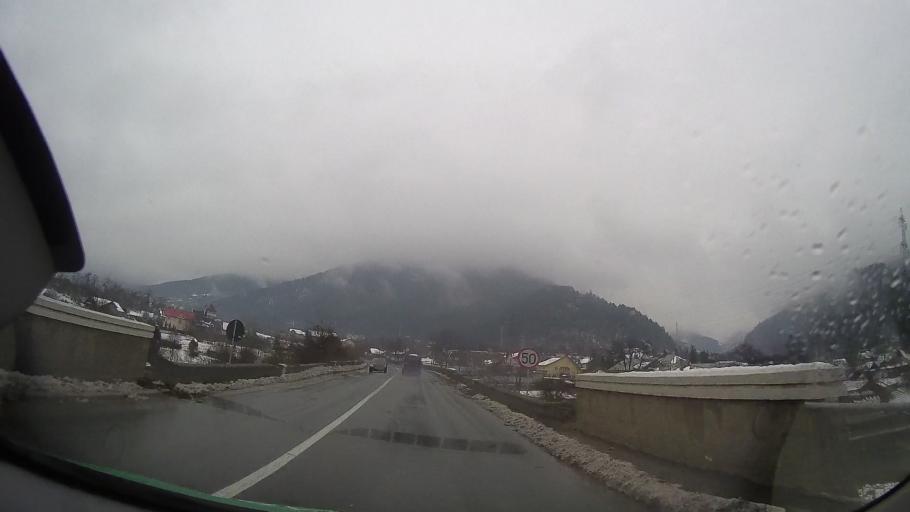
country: RO
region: Neamt
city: Viisoara
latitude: 46.9307
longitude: 26.2211
